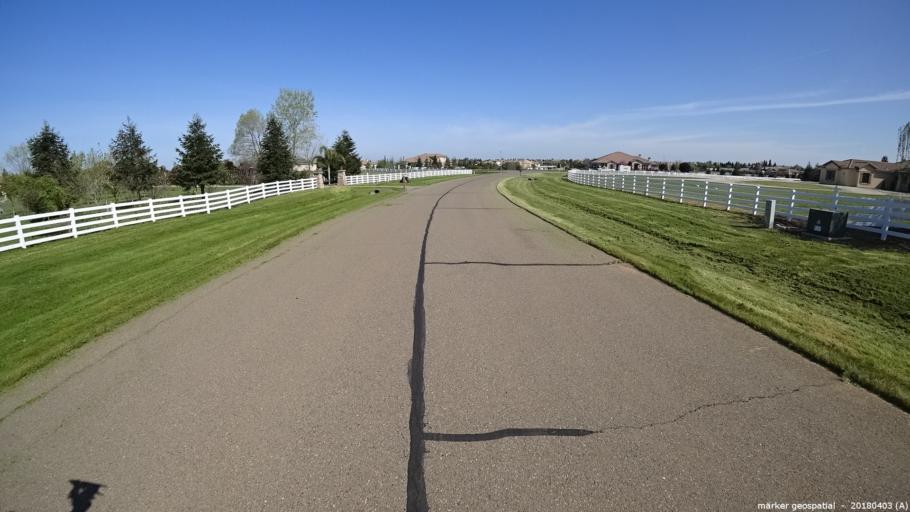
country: US
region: California
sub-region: Sacramento County
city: Clay
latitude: 38.4047
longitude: -121.1927
